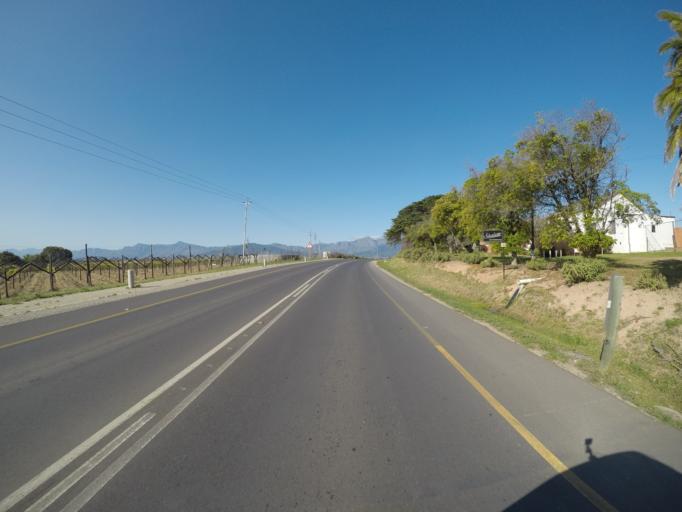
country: ZA
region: Western Cape
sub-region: Cape Winelands District Municipality
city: Noorder-Paarl
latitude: -33.6702
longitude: 18.9243
